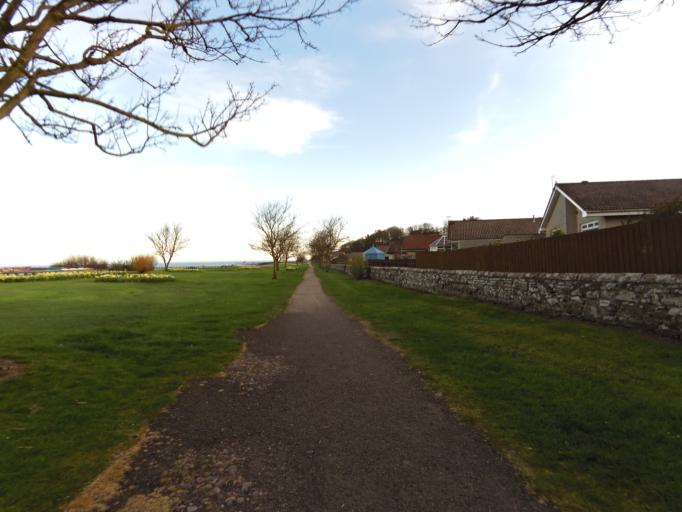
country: GB
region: Scotland
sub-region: Aberdeenshire
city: Inverbervie
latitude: 56.8426
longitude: -2.2763
